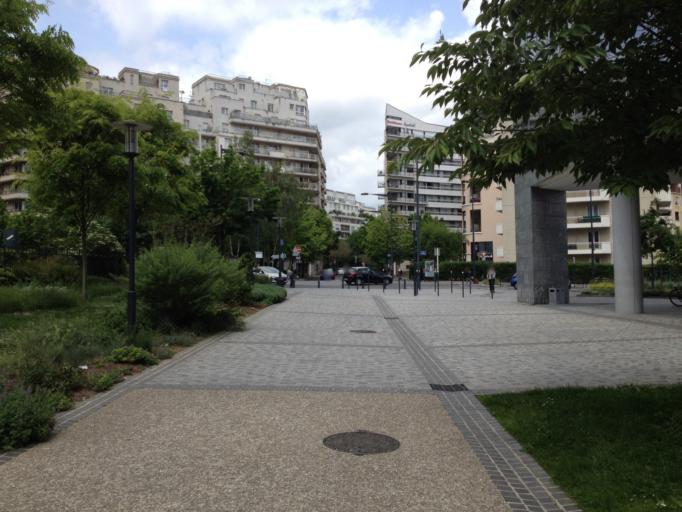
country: FR
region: Ile-de-France
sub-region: Departement des Hauts-de-Seine
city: La Defense
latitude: 48.8970
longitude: 2.2394
